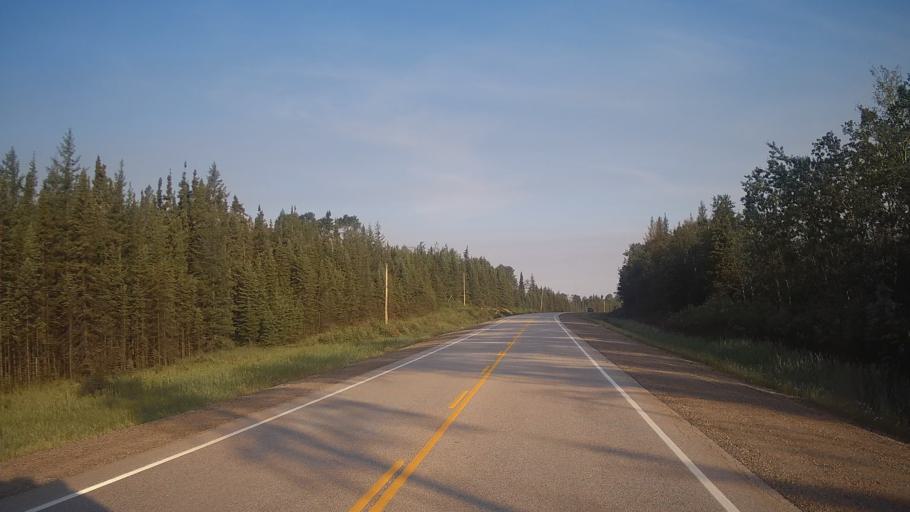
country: CA
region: Ontario
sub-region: Rainy River District
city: Atikokan
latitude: 49.2546
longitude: -91.1202
